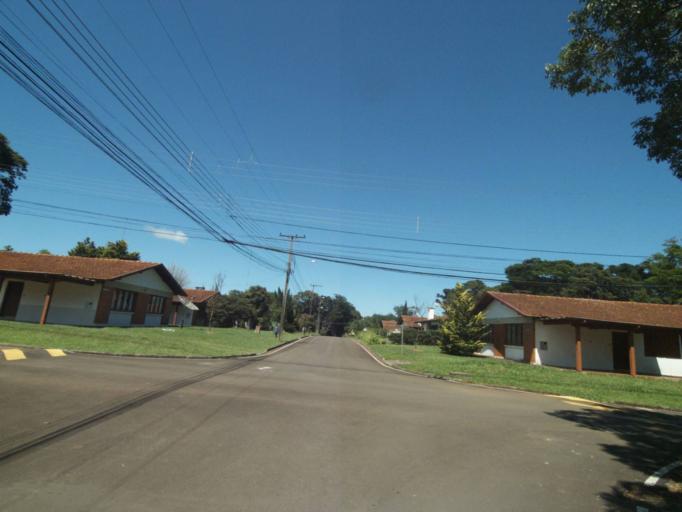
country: BR
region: Parana
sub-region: Chopinzinho
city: Chopinzinho
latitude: -25.7977
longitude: -52.0957
